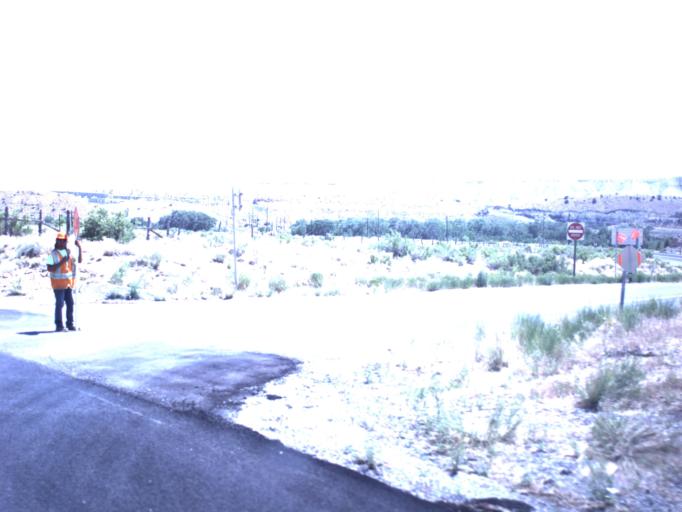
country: US
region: Utah
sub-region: Emery County
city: Orangeville
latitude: 39.2543
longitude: -111.0972
